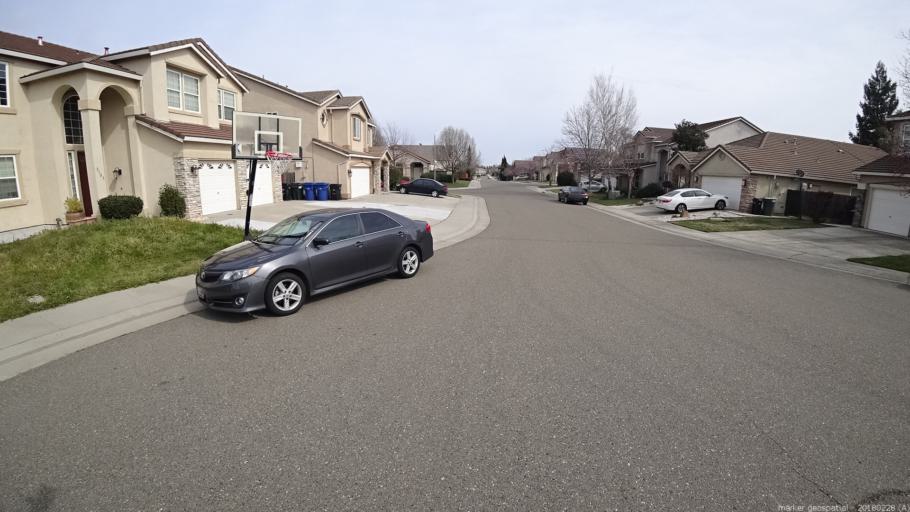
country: US
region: California
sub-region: Sacramento County
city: Antelope
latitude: 38.7095
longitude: -121.3458
